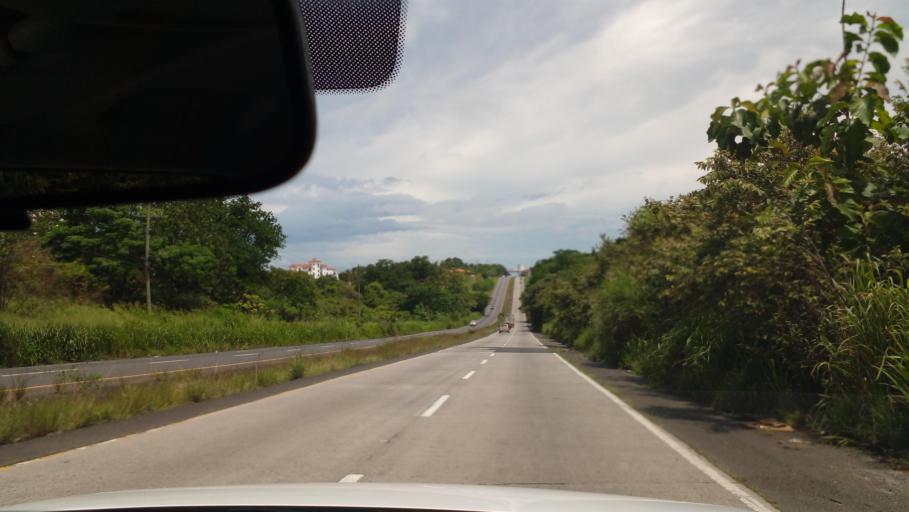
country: PA
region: Panama
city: Nueva Gorgona
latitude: 8.4954
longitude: -79.9582
